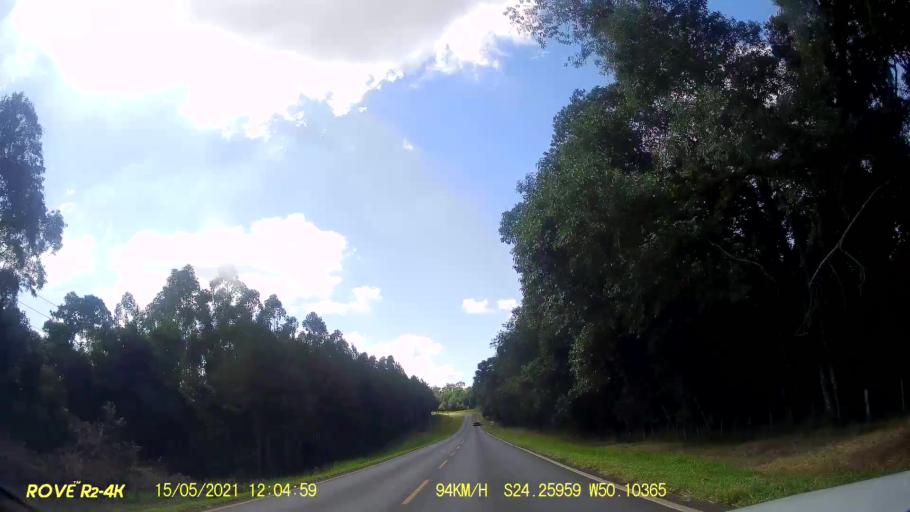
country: BR
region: Parana
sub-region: Pirai Do Sul
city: Pirai do Sul
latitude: -24.2597
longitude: -50.1037
